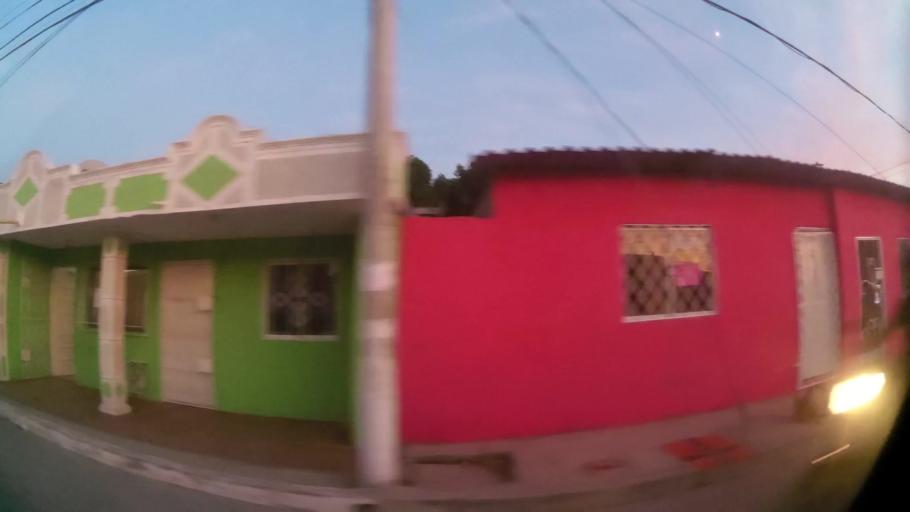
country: CO
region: Atlantico
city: Barranquilla
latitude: 10.9493
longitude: -74.8265
